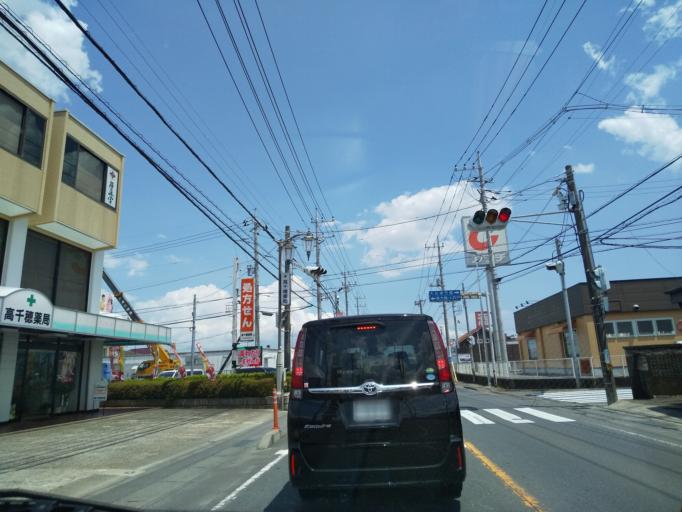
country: JP
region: Ibaraki
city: Ishioka
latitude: 36.1862
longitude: 140.2989
